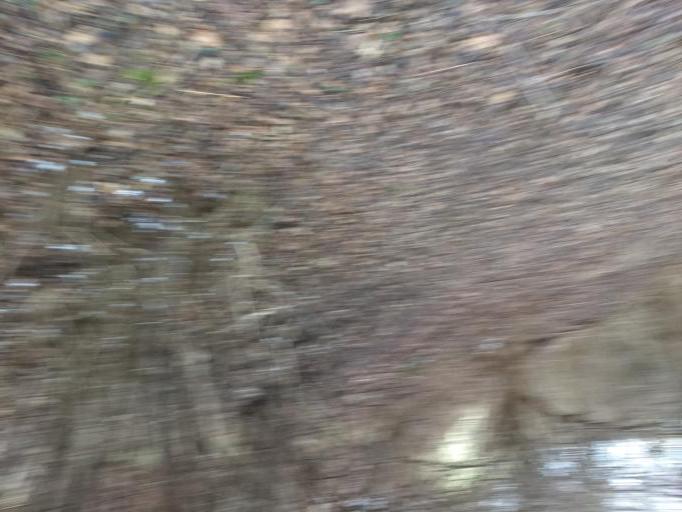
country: US
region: Pennsylvania
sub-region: Allegheny County
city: Bloomfield
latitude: 40.4246
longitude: -79.9504
